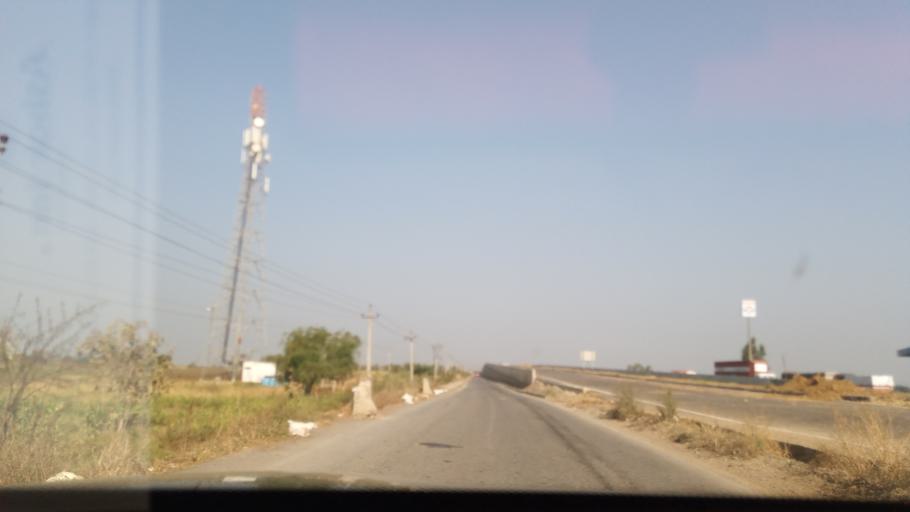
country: IN
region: Karnataka
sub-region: Haveri
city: Savanur
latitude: 14.8799
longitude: 75.3103
